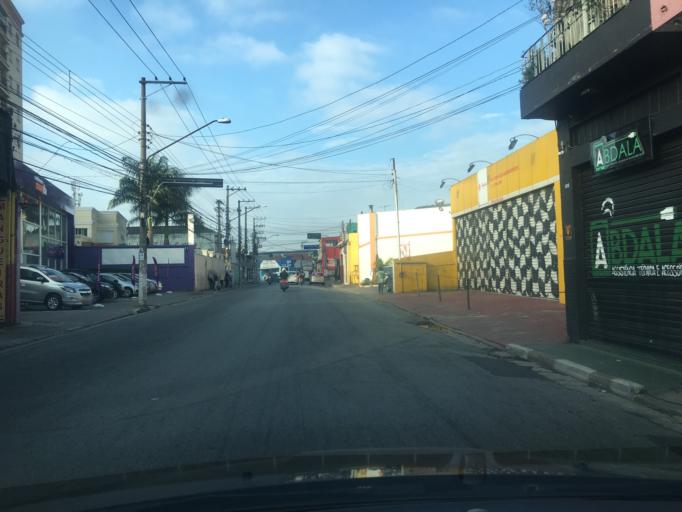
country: BR
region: Sao Paulo
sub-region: Guarulhos
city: Guarulhos
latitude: -23.5028
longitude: -46.5516
